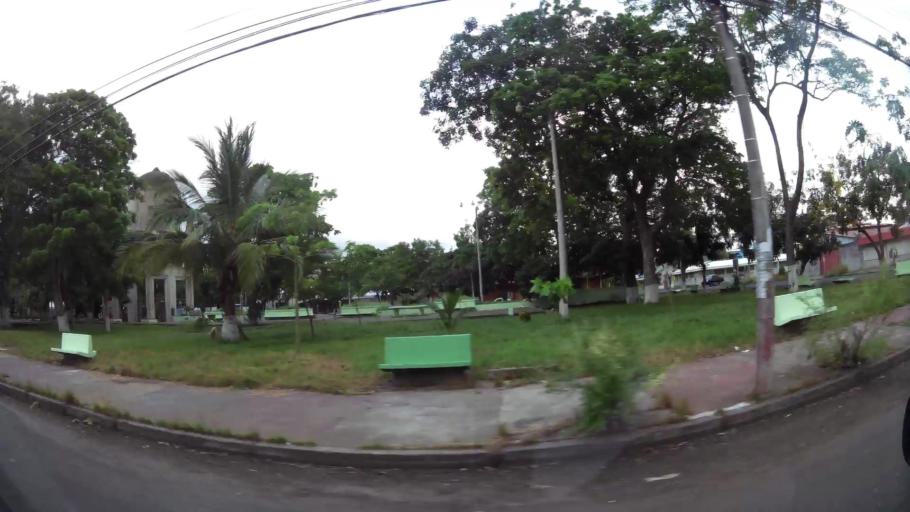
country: CR
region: Puntarenas
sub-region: Canton Central de Puntarenas
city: Puntarenas
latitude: 9.9782
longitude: -84.8369
